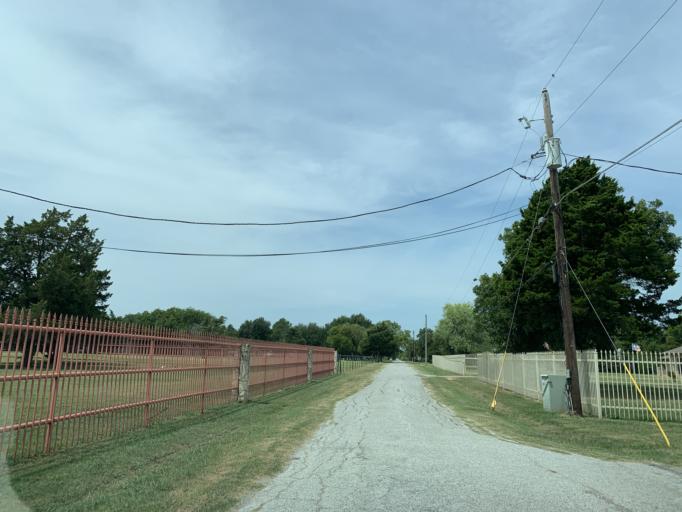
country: US
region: Texas
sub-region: Dallas County
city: Cedar Hill
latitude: 32.6544
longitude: -97.0005
